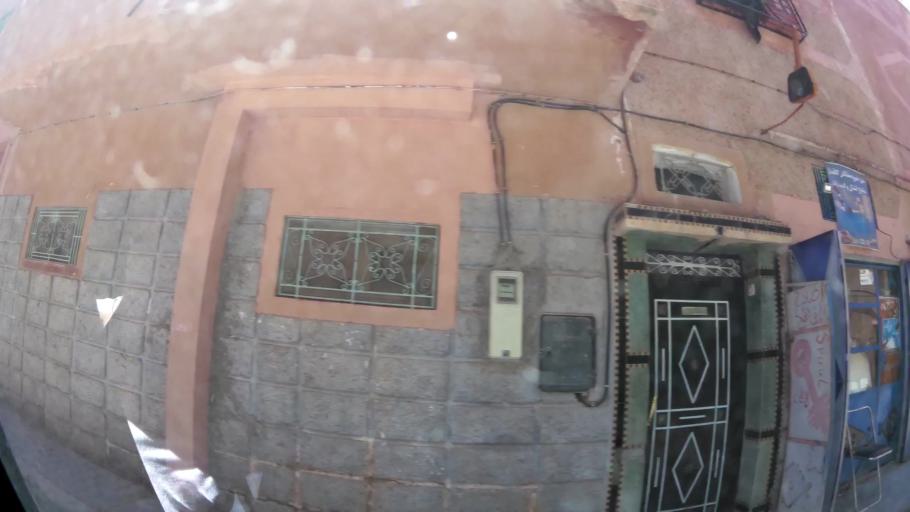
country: MA
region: Marrakech-Tensift-Al Haouz
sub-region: Marrakech
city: Marrakesh
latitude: 31.6577
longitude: -8.0015
